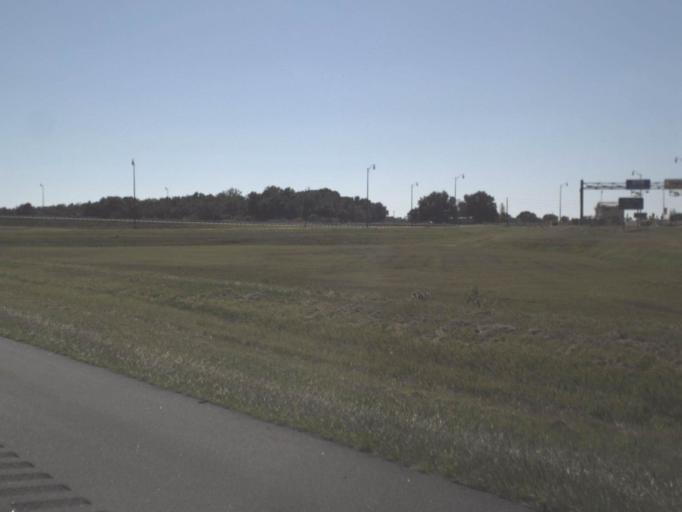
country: US
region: Florida
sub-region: Lake County
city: Hawthorne
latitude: 28.7585
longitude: -81.9422
